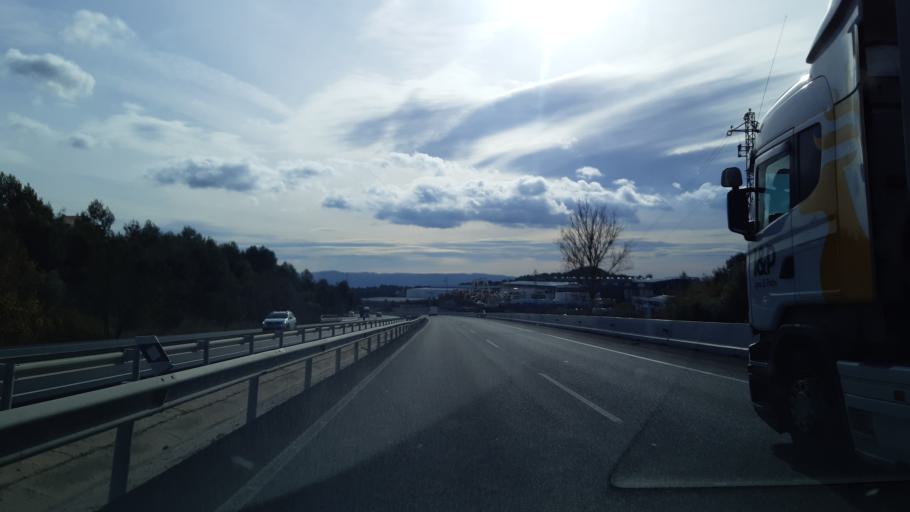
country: ES
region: Catalonia
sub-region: Provincia de Barcelona
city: Collbato
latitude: 41.5793
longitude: 1.7786
